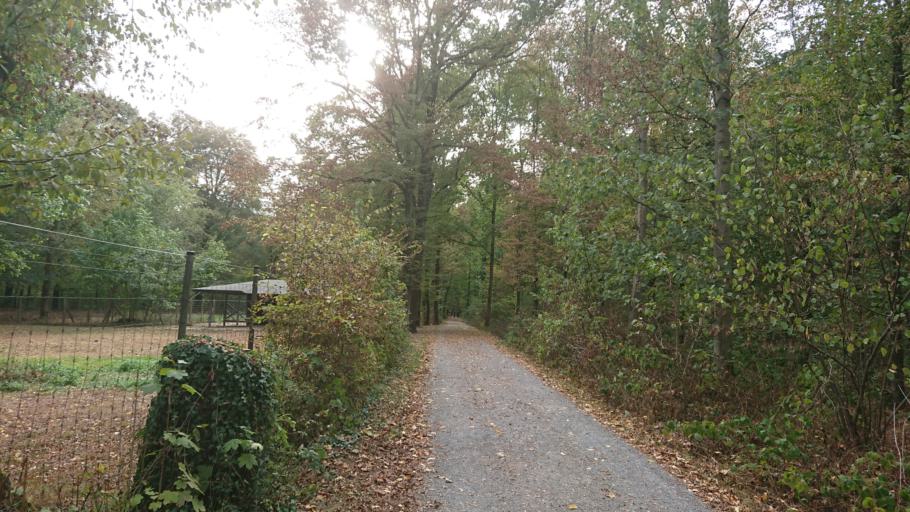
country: DE
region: Baden-Wuerttemberg
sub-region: Karlsruhe Region
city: Karlsruhe
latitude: 48.9893
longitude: 8.4233
